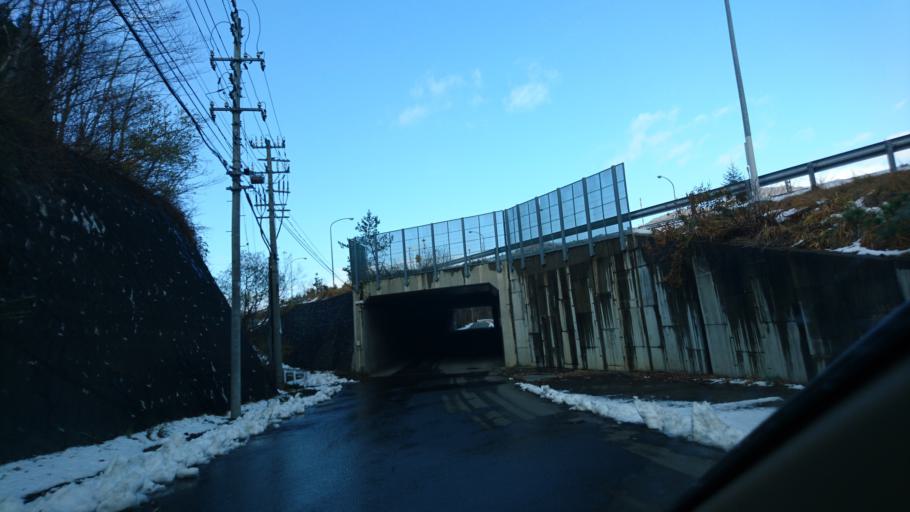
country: JP
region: Iwate
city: Kitakami
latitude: 39.2918
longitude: 140.8396
